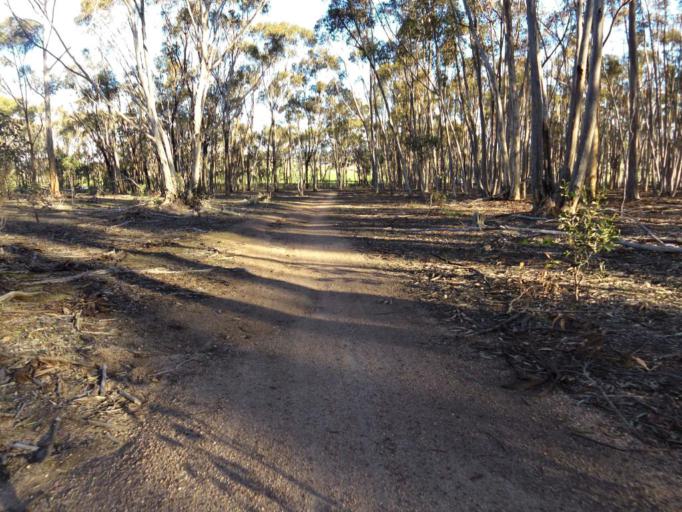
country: AU
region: Victoria
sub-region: Greater Geelong
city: Lara
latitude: -37.9640
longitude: 144.4075
